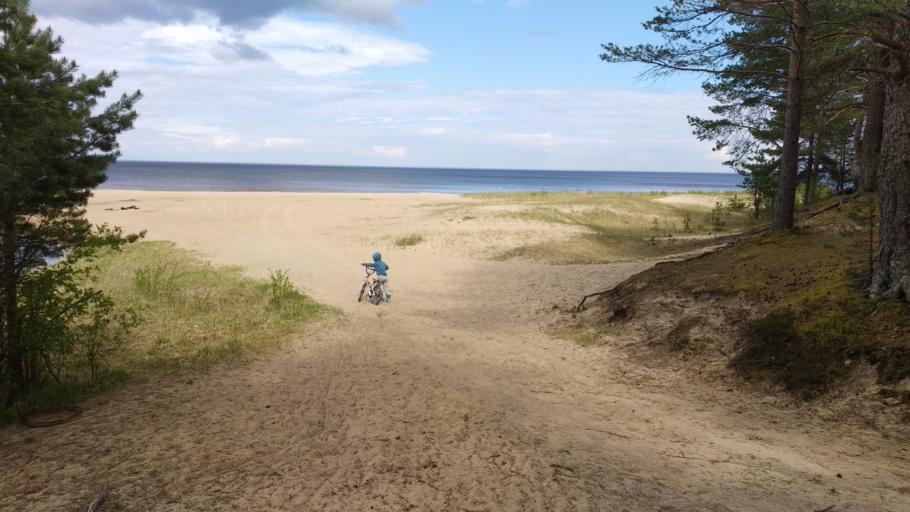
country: RU
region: Republic of Karelia
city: Sheltozero
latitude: 61.3795
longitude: 35.3645
